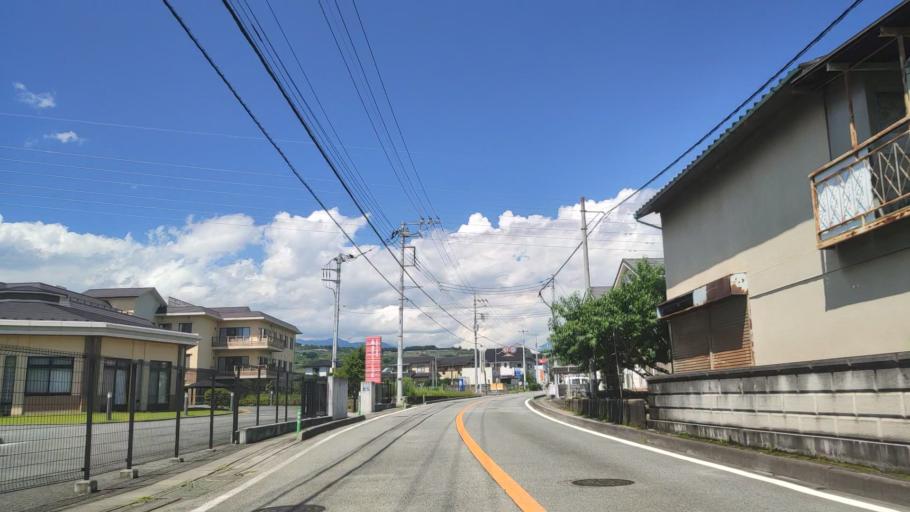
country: JP
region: Yamanashi
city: Isawa
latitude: 35.6781
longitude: 138.6581
